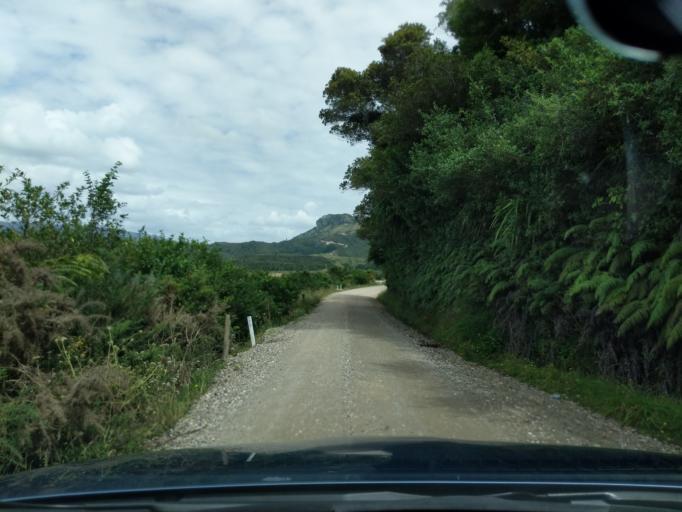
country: NZ
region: Tasman
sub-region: Tasman District
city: Takaka
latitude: -40.6530
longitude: 172.4588
